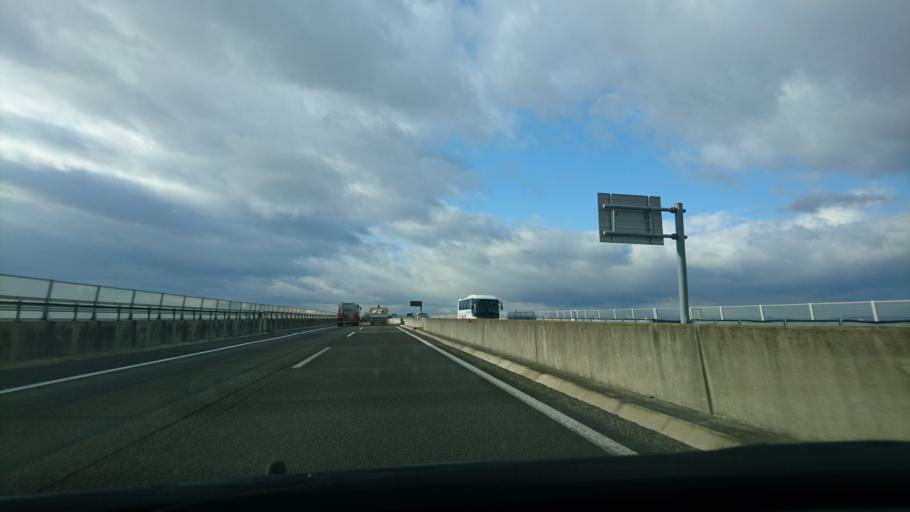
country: JP
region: Miyagi
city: Rifu
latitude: 38.2672
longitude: 140.9750
